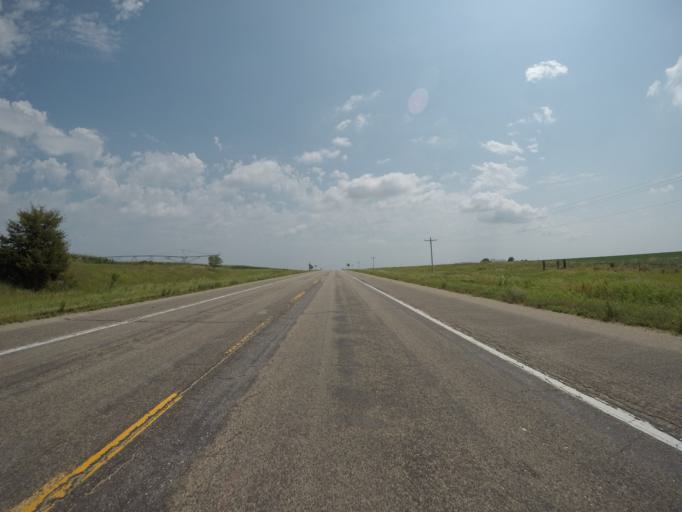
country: US
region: Nebraska
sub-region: Clay County
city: Clay Center
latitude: 40.4280
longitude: -98.0515
